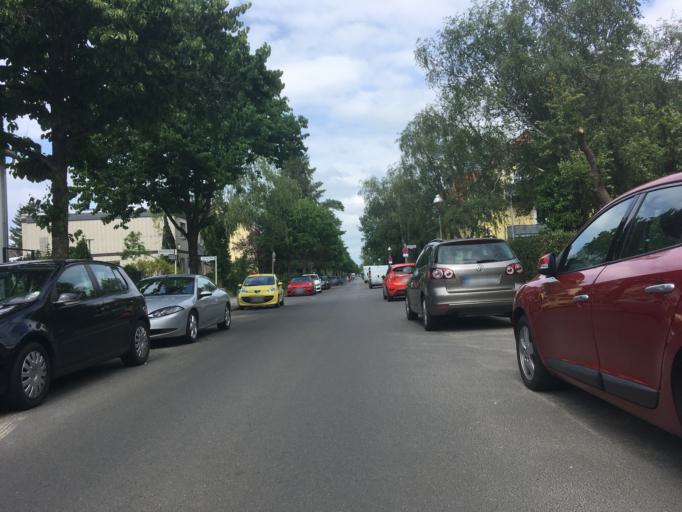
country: DE
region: Berlin
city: Lichtenrade
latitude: 52.4071
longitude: 13.3910
